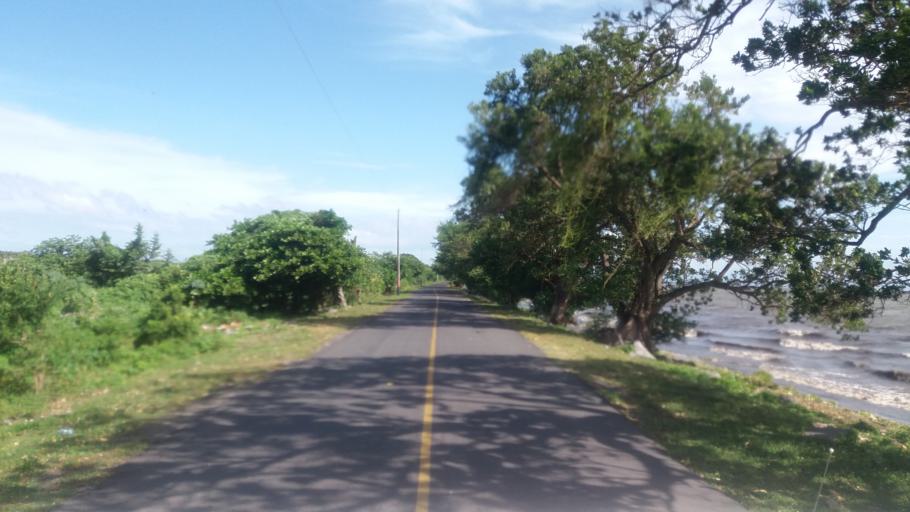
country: NI
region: Granada
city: Granada
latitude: 11.9699
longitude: -85.9434
